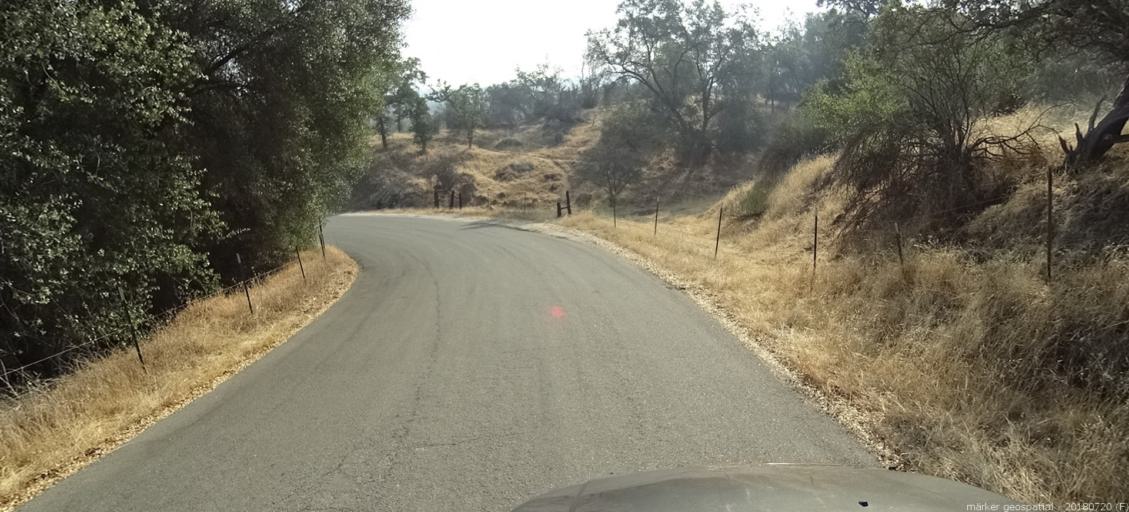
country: US
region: California
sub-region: Madera County
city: Yosemite Lakes
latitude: 37.2768
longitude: -119.8731
